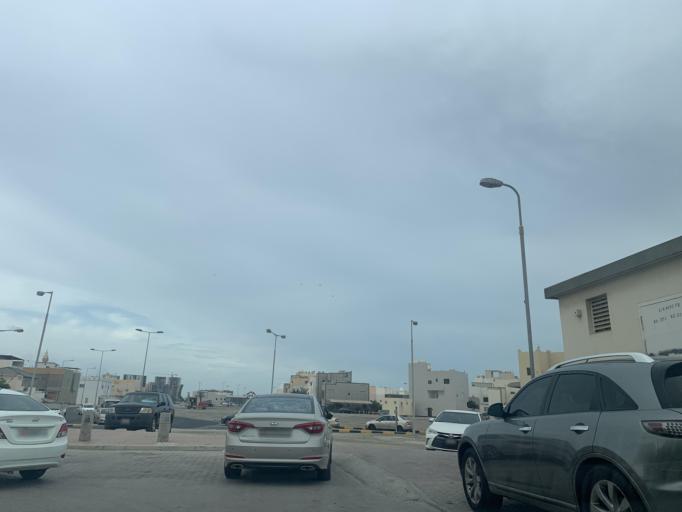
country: BH
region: Muharraq
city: Al Hadd
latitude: 26.2724
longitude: 50.6566
